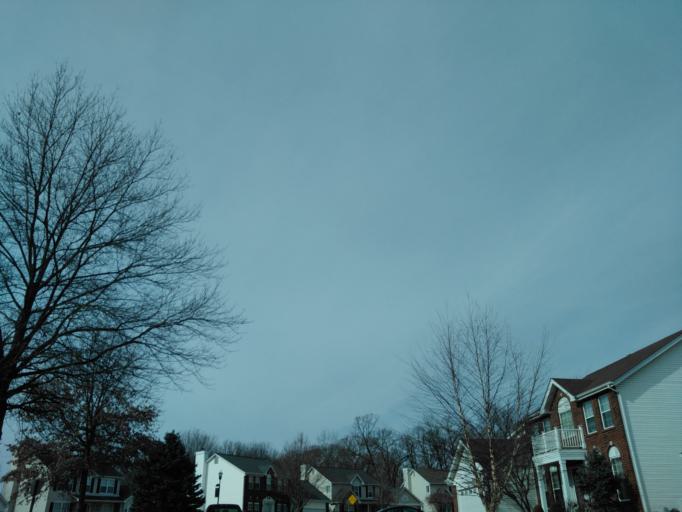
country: US
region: Missouri
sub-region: Saint Louis County
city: Valley Park
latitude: 38.5489
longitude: -90.5190
